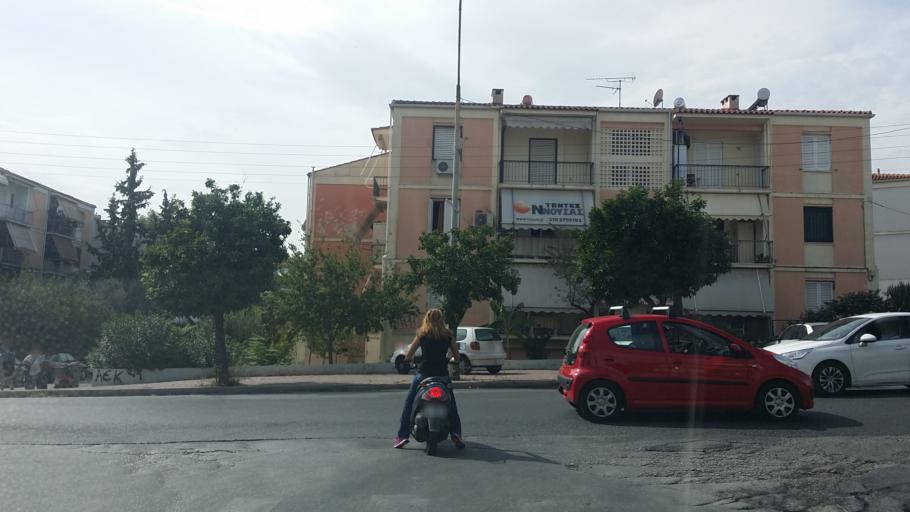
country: GR
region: Attica
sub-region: Nomarchia Athinas
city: Nea Ionia
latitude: 38.0494
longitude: 23.7499
